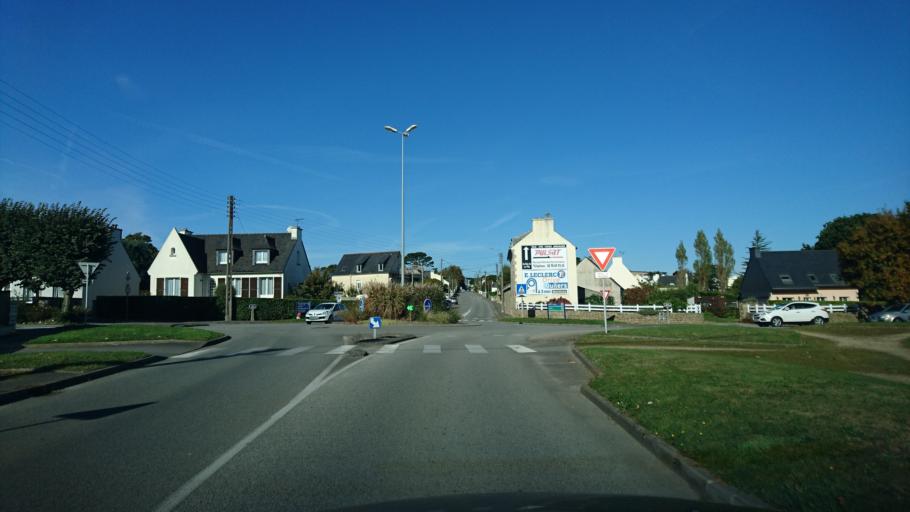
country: FR
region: Brittany
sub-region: Departement du Finistere
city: Saint-Renan
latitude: 48.4263
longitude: -4.6149
